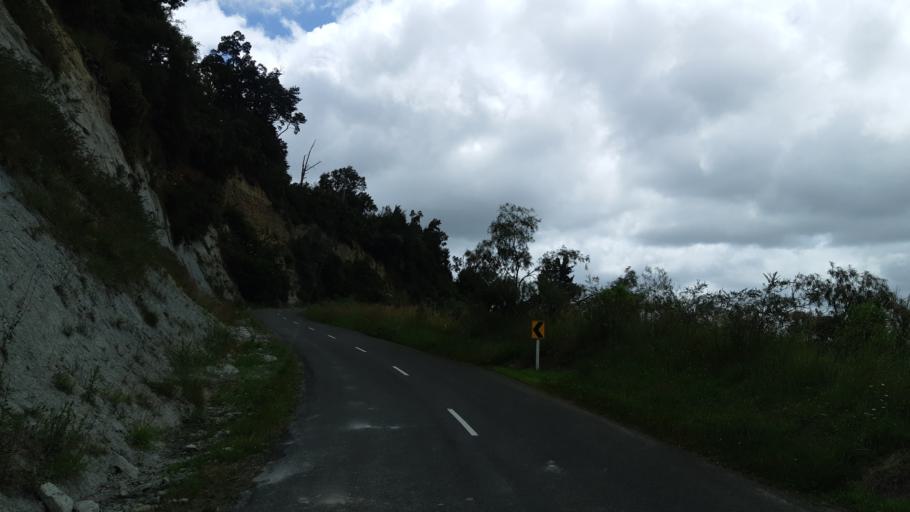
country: NZ
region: Manawatu-Wanganui
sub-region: Palmerston North City
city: Palmerston North
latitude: -39.9395
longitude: 175.9167
